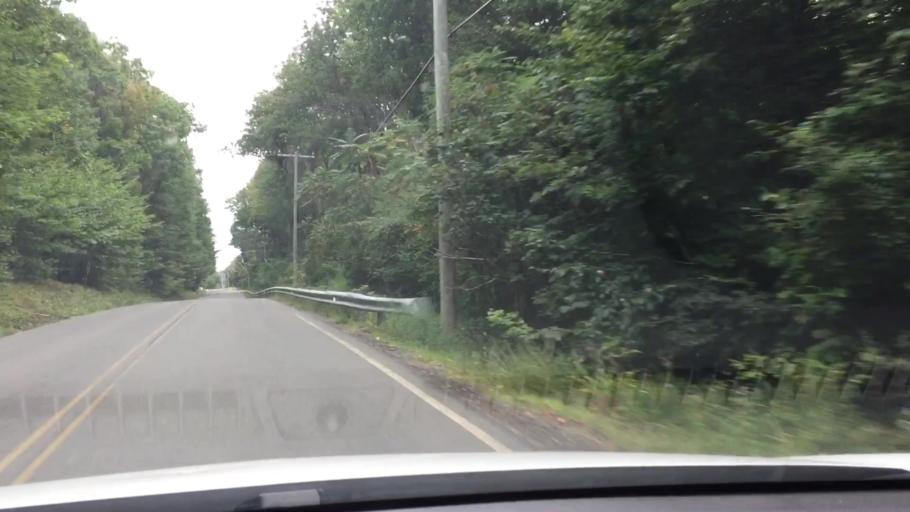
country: US
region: Massachusetts
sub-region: Berkshire County
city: Otis
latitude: 42.2077
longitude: -72.9415
